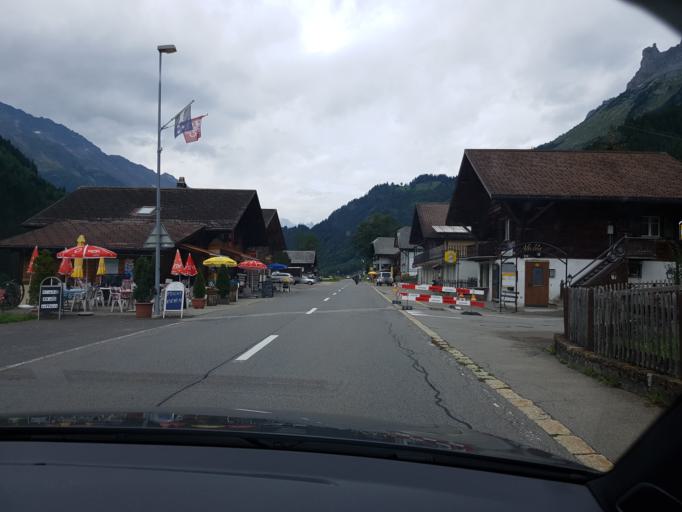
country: CH
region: Obwalden
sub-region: Obwalden
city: Engelberg
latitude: 46.7378
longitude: 8.3522
